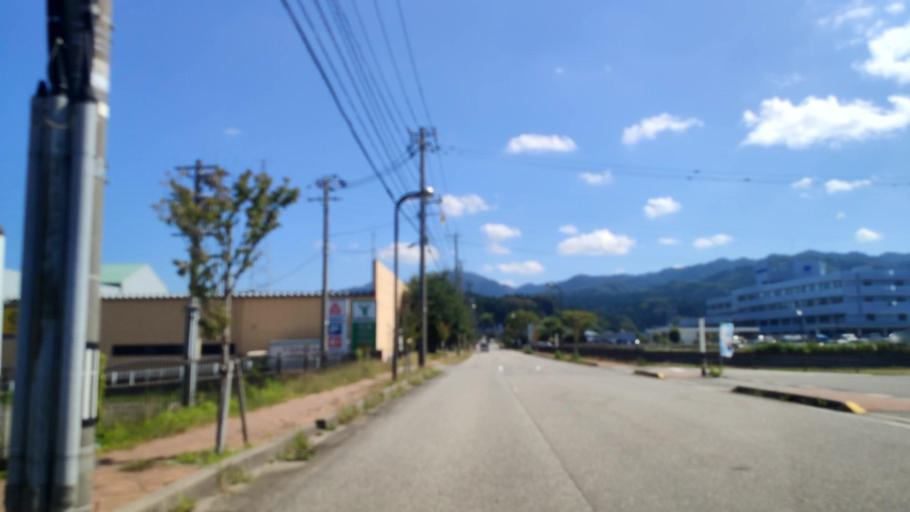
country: JP
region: Ishikawa
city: Nanao
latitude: 37.3851
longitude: 136.9029
